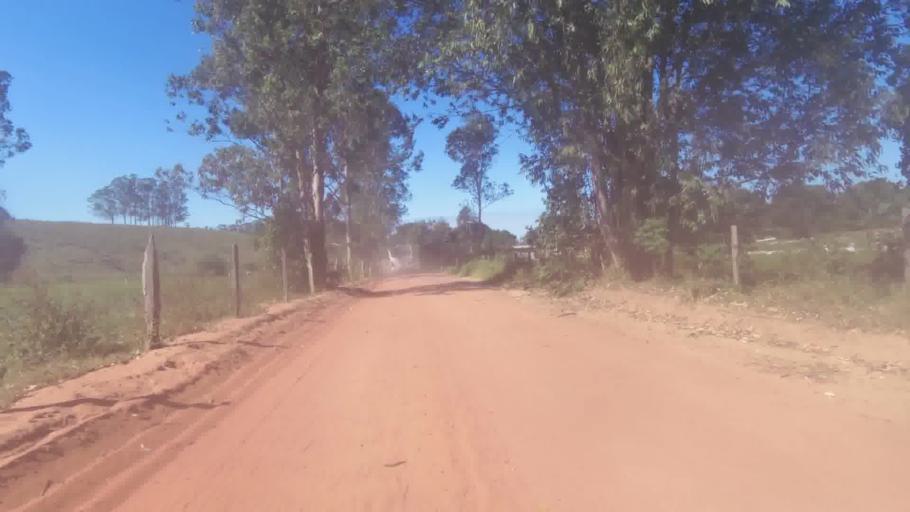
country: BR
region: Espirito Santo
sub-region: Marataizes
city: Marataizes
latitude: -21.1229
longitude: -40.9760
